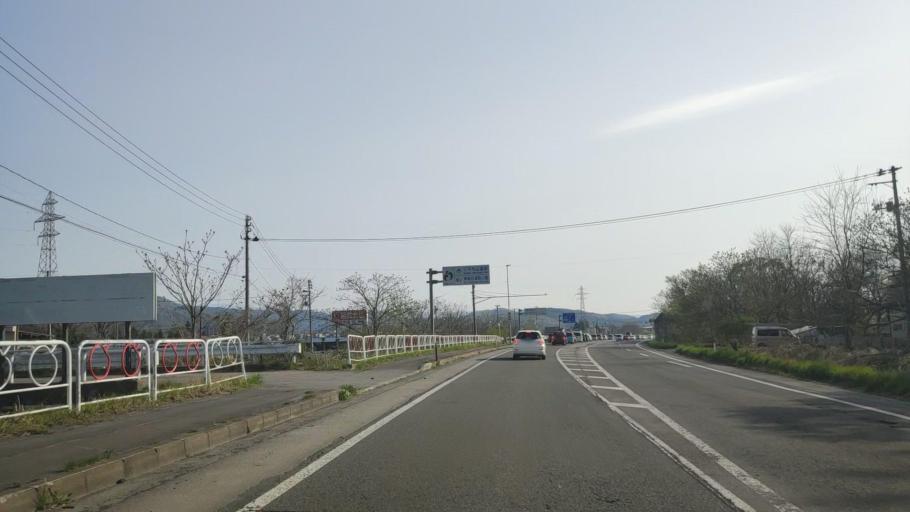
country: JP
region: Aomori
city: Aomori Shi
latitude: 40.8482
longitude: 140.8372
